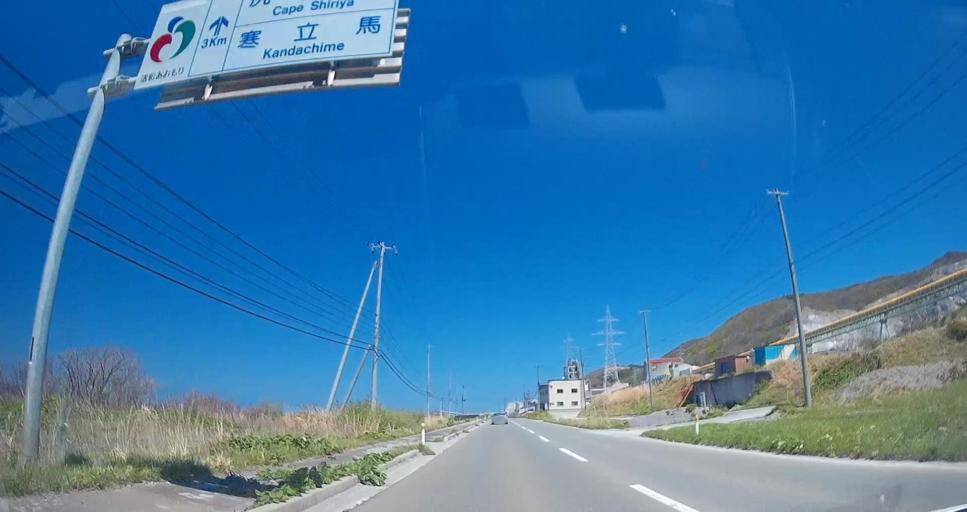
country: JP
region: Aomori
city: Mutsu
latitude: 41.4021
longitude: 141.4280
